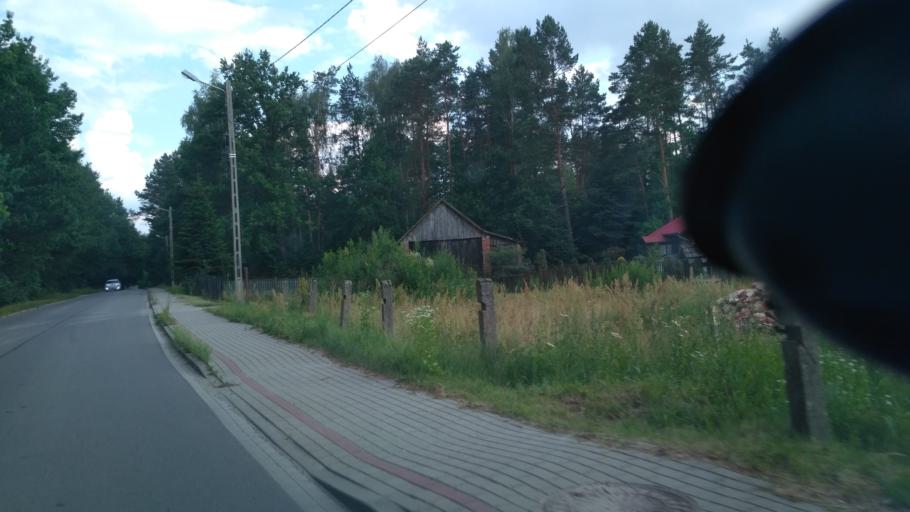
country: PL
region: Subcarpathian Voivodeship
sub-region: Powiat rzeszowski
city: Wysoka Glogowska
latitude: 50.1334
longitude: 22.0219
